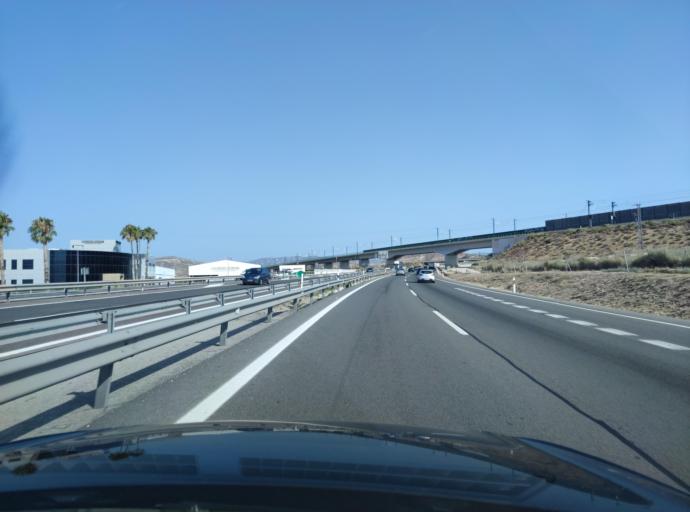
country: ES
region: Valencia
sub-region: Provincia de Alicante
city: Novelda
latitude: 38.4088
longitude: -0.7771
